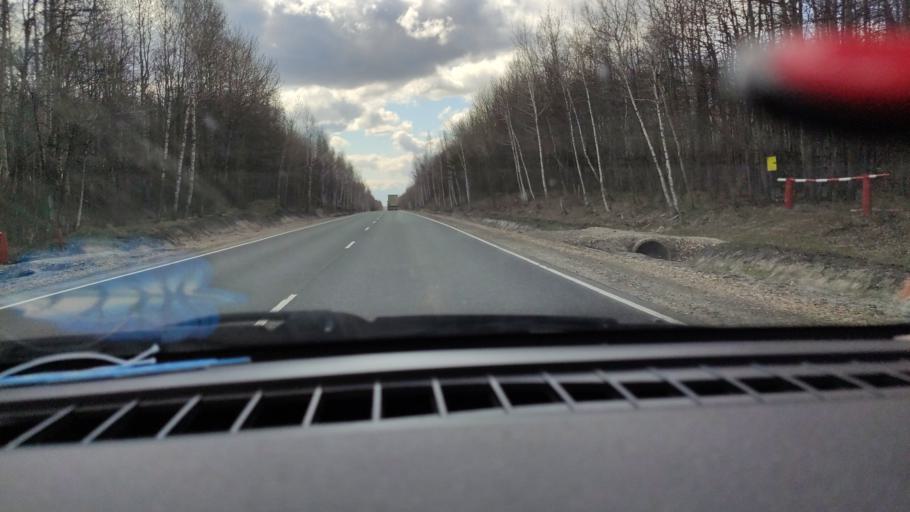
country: RU
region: Saratov
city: Khvalynsk
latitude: 52.4362
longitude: 48.0093
